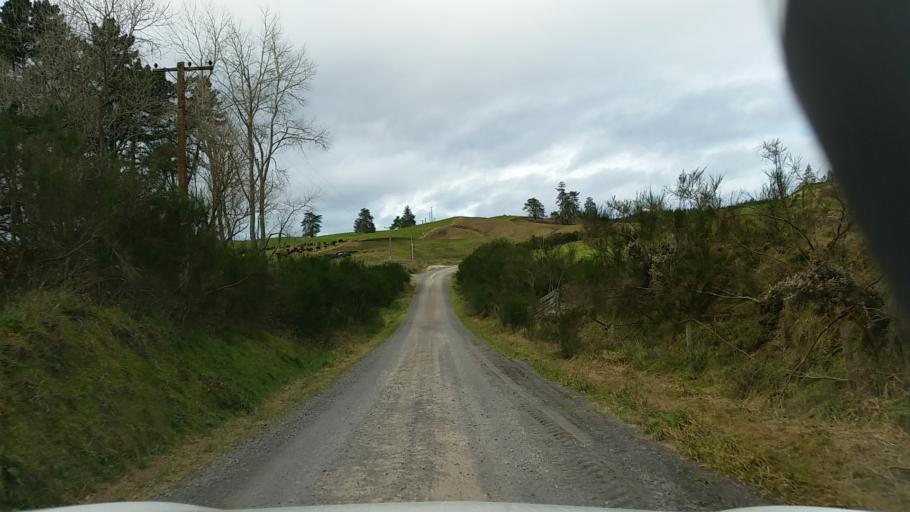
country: NZ
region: Bay of Plenty
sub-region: Whakatane District
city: Murupara
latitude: -38.3371
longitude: 176.5379
